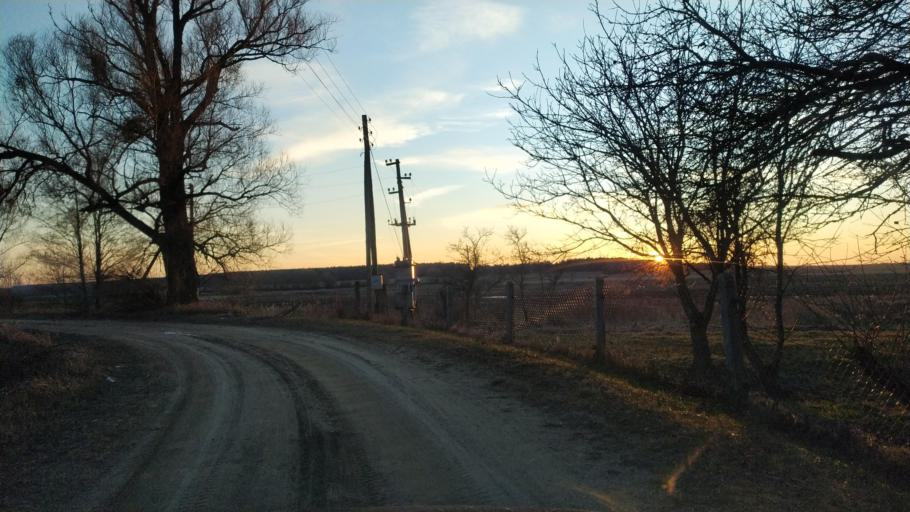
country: BY
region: Brest
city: Pruzhany
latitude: 52.5498
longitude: 24.2499
